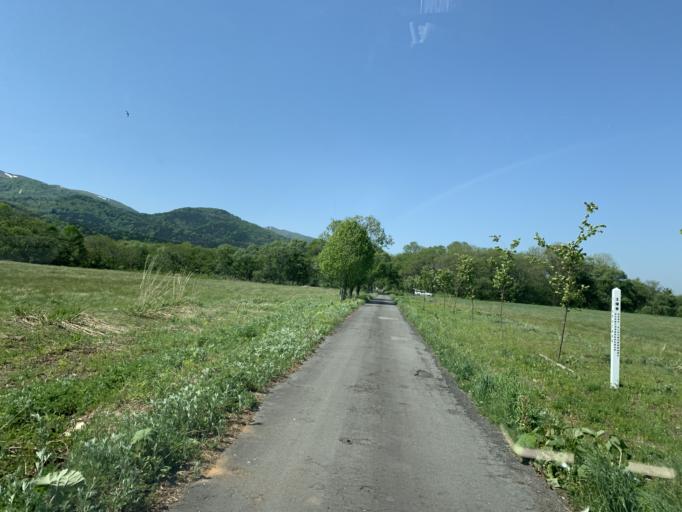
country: JP
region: Iwate
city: Shizukuishi
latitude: 39.5498
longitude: 140.8211
